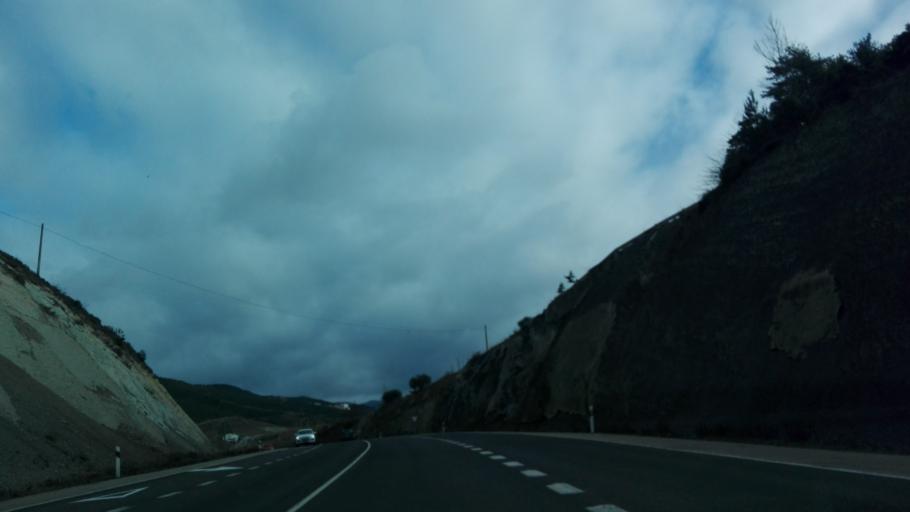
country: ES
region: Navarre
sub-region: Provincia de Navarra
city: Egues-Uharte
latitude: 42.8386
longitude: -1.5959
